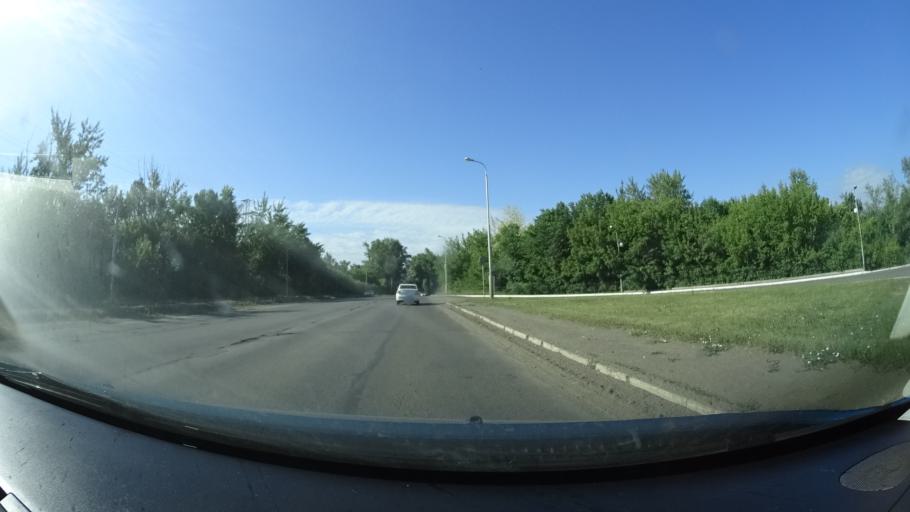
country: RU
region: Bashkortostan
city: Ufa
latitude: 54.8460
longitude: 56.0765
